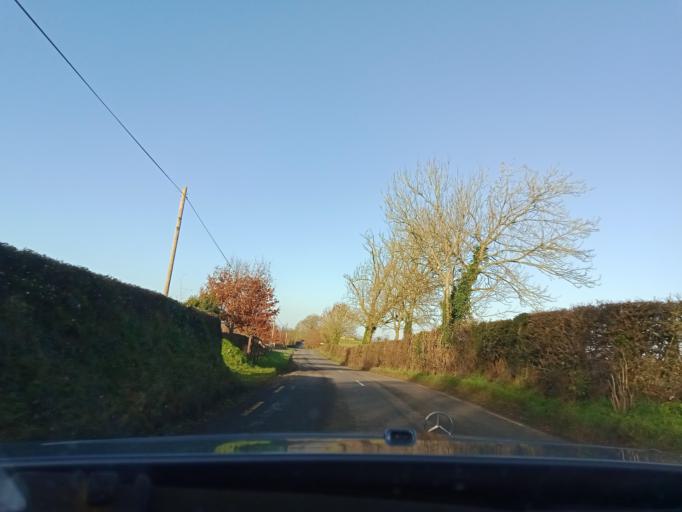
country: IE
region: Leinster
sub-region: Kilkenny
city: Callan
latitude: 52.5042
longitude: -7.3829
